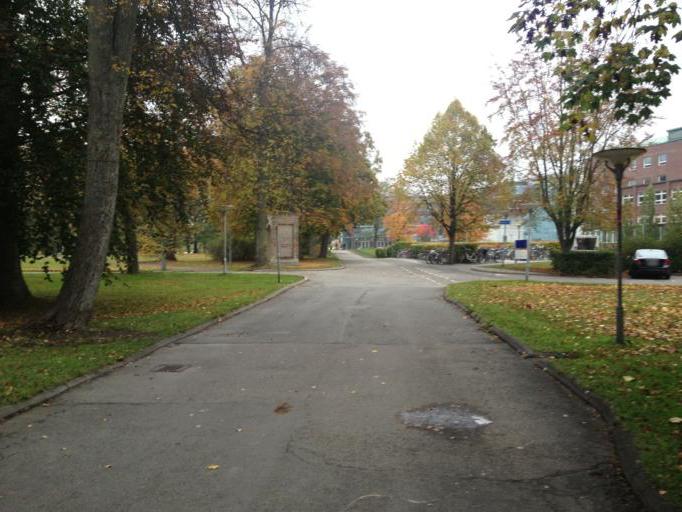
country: SE
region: Skane
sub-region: Lunds Kommun
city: Lund
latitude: 55.7133
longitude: 13.2108
